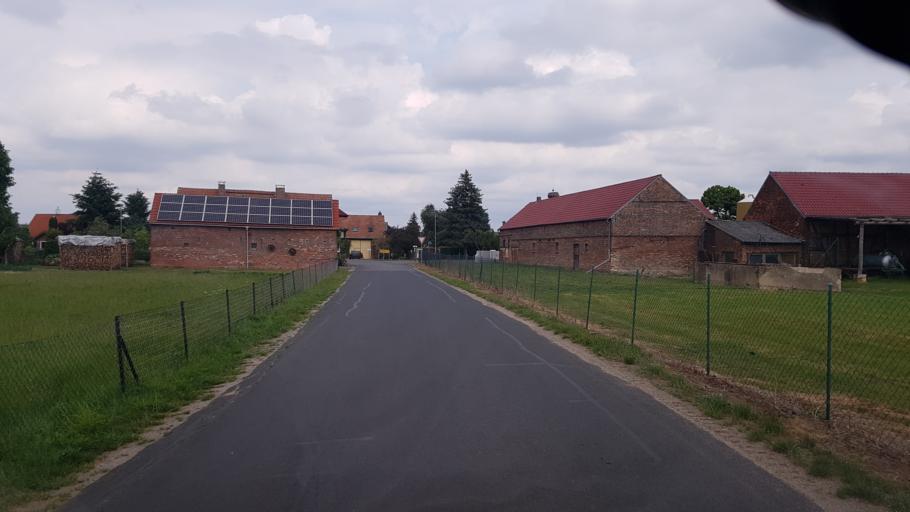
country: DE
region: Brandenburg
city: Lebusa
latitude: 51.8239
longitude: 13.4546
